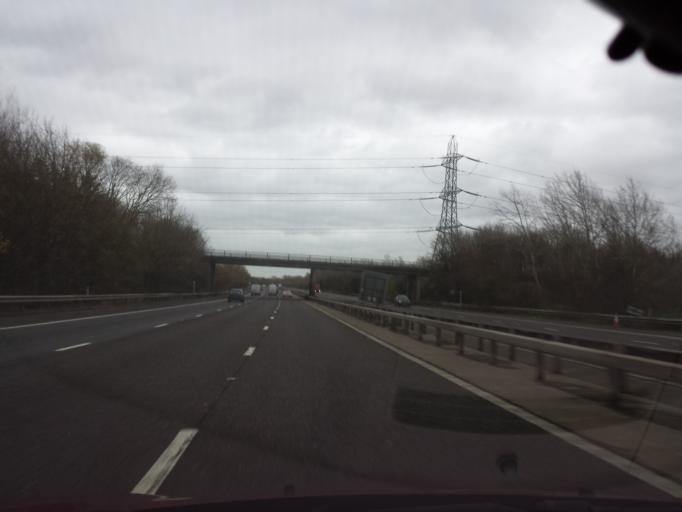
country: GB
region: England
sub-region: Surrey
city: Addlestone
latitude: 51.3938
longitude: -0.4799
